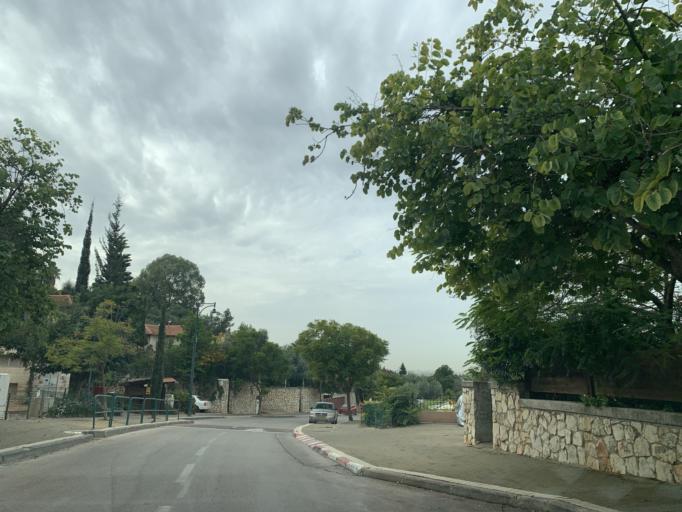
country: IL
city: Nirit
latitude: 32.1480
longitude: 34.9845
